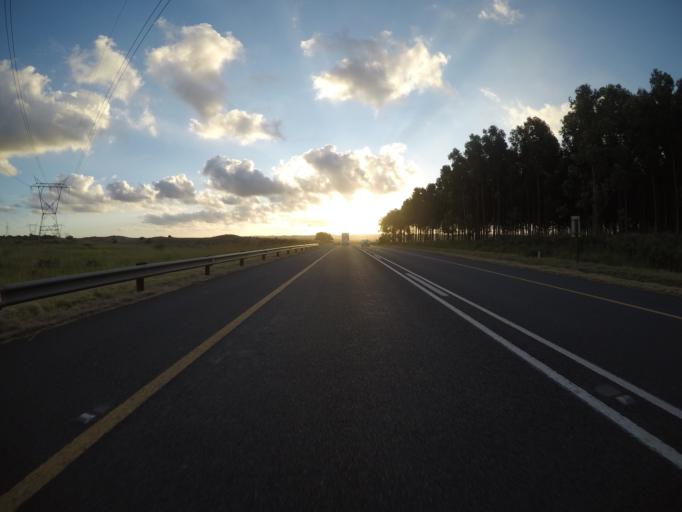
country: ZA
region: KwaZulu-Natal
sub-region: uThungulu District Municipality
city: Richards Bay
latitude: -28.6954
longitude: 32.0220
